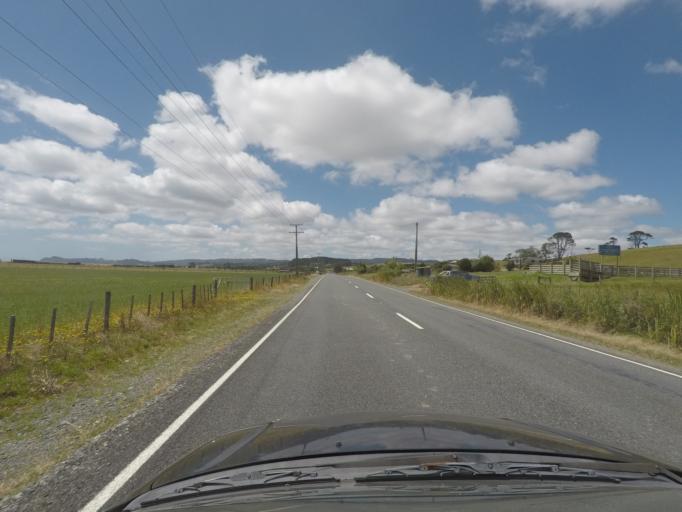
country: NZ
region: Northland
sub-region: Whangarei
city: Ruakaka
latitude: -36.0063
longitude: 174.4789
